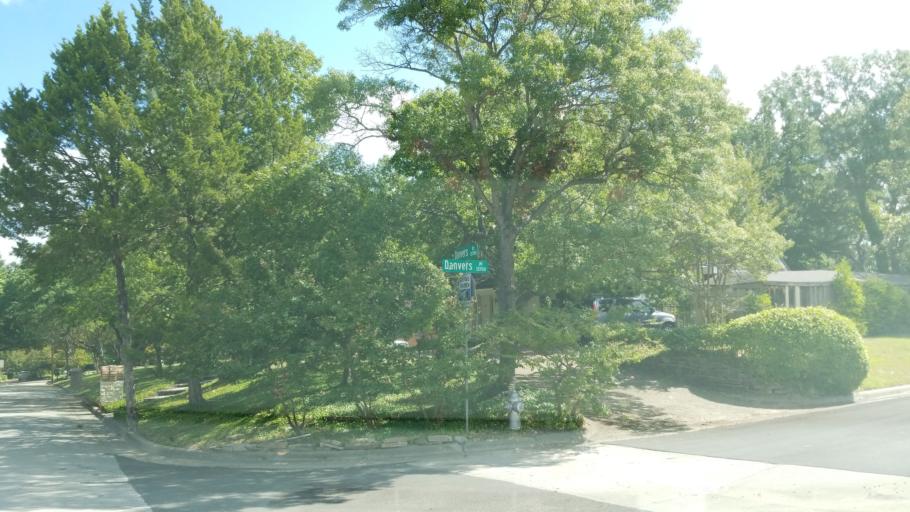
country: US
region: Texas
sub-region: Dallas County
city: Addison
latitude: 32.9345
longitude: -96.7998
